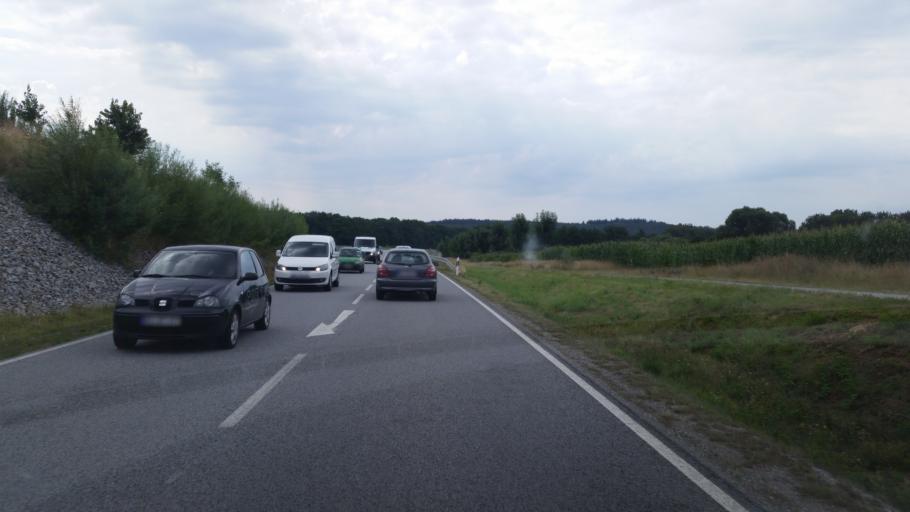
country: DE
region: Saxony
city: Elstra
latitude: 51.2231
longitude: 14.1490
